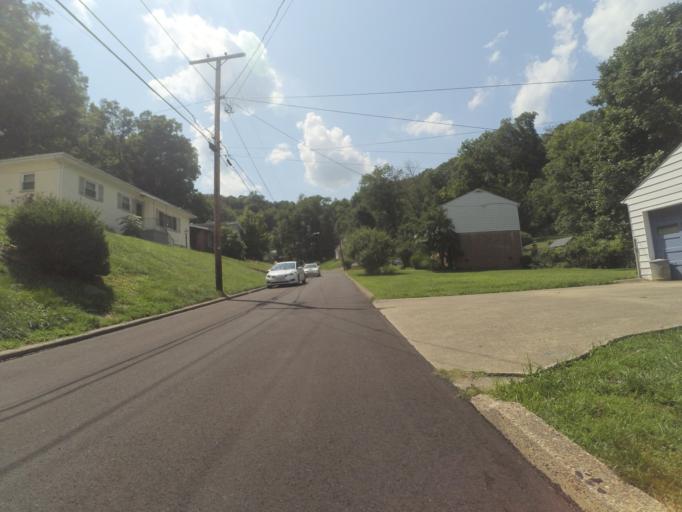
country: US
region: West Virginia
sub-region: Cabell County
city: Huntington
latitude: 38.3974
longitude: -82.4287
